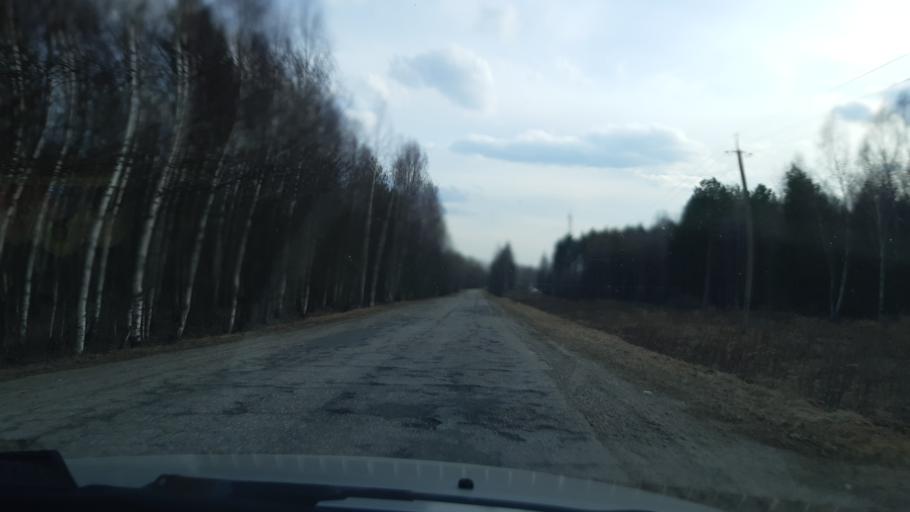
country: RU
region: Vladimir
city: Nikologory
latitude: 56.1117
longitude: 41.9835
